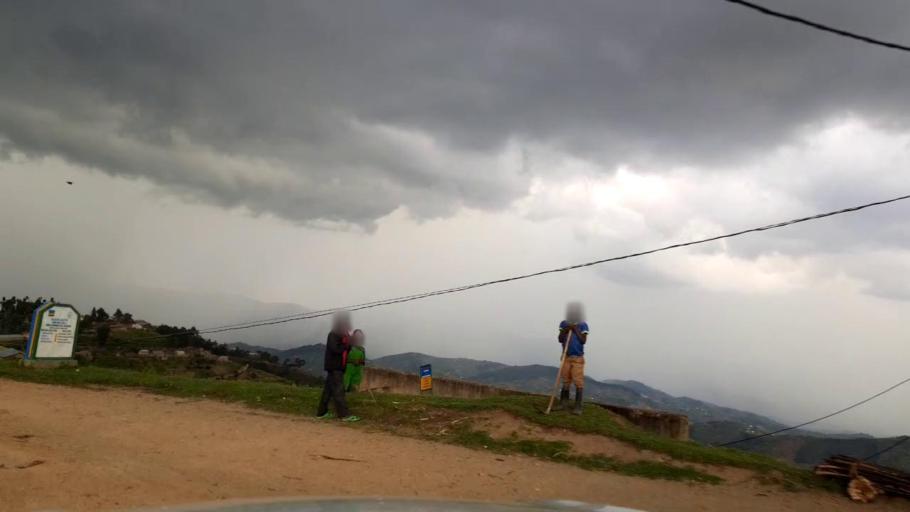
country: RW
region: Southern Province
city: Gitarama
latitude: -1.8730
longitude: 29.5868
